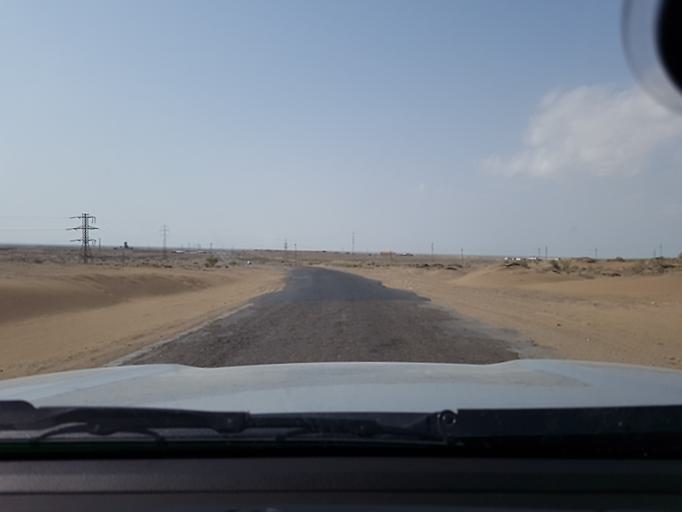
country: TM
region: Balkan
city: Gumdag
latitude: 39.1274
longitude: 54.5777
